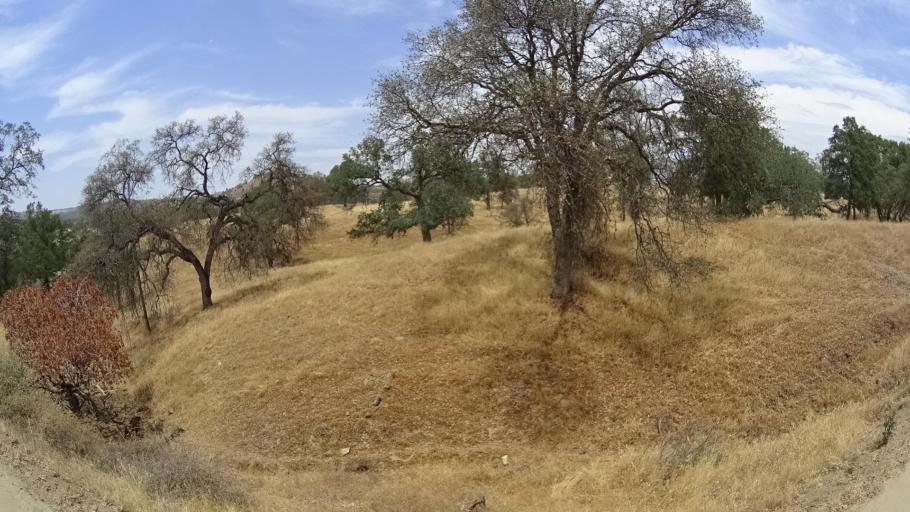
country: US
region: California
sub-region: Madera County
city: Ahwahnee
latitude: 37.3456
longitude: -119.8739
